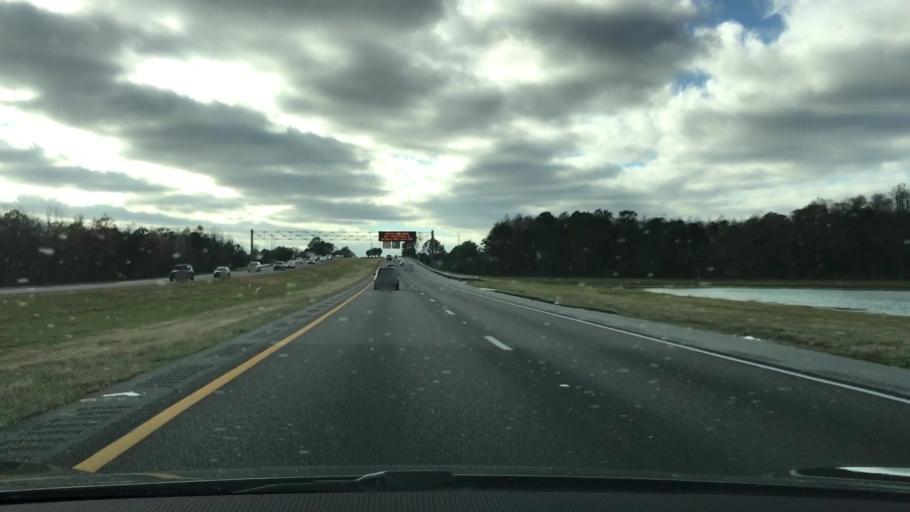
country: US
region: Florida
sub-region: Orange County
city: Hunters Creek
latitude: 28.3587
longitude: -81.4459
